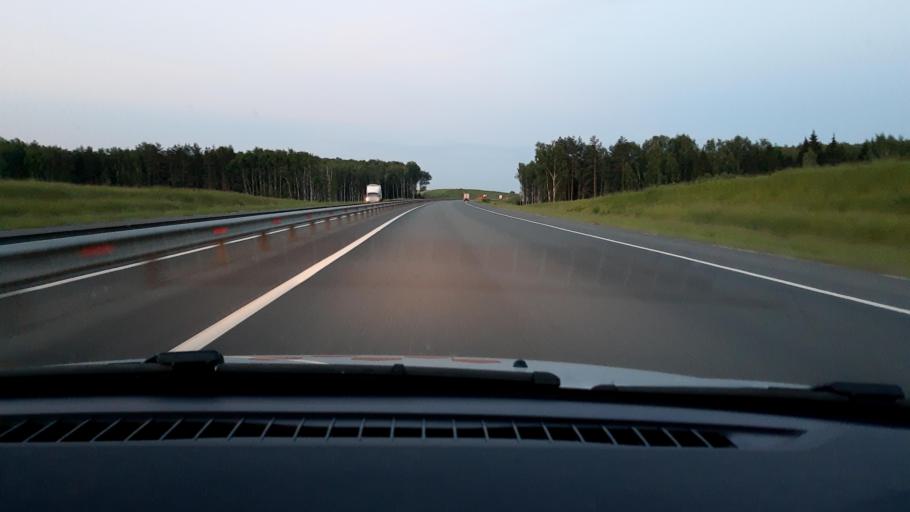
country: RU
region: Nizjnij Novgorod
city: Kstovo
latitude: 56.0983
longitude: 44.0630
